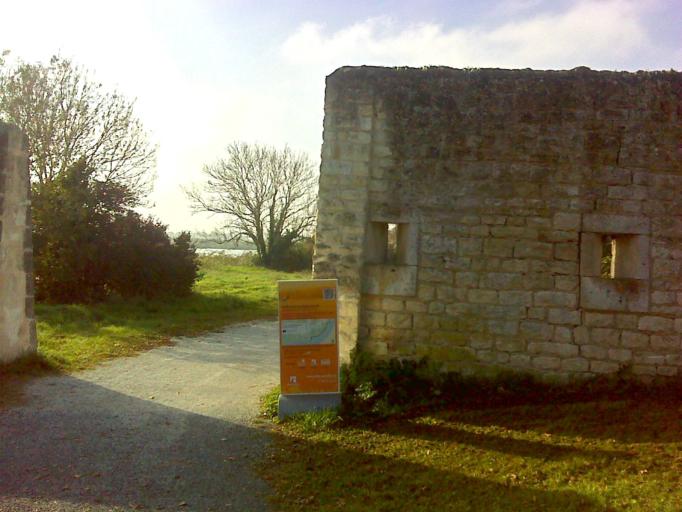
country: FR
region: Poitou-Charentes
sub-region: Departement de la Charente-Maritime
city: Echillais
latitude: 45.9249
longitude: -0.9493
